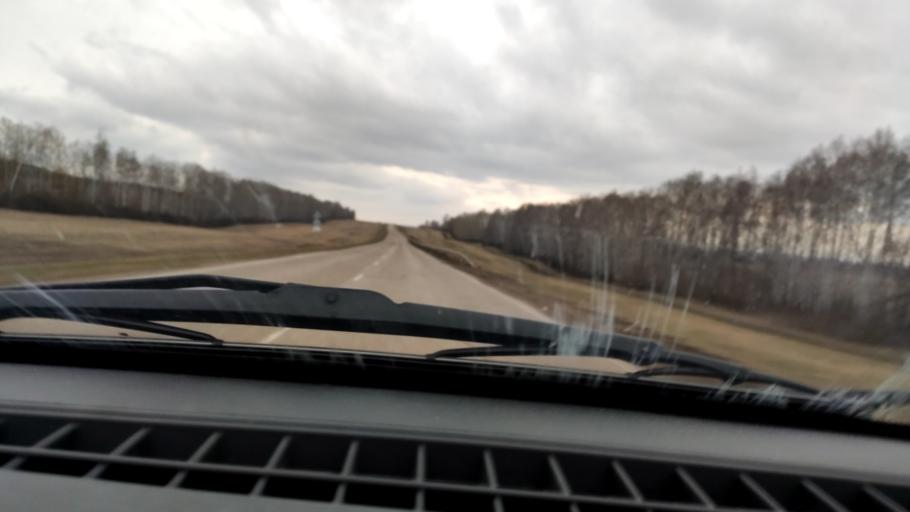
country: RU
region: Bashkortostan
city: Chekmagush
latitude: 55.1326
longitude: 54.4778
